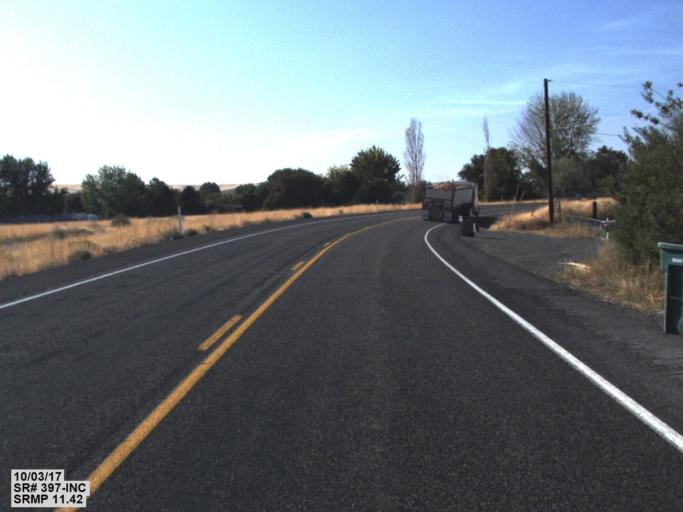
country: US
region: Washington
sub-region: Benton County
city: Finley
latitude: 46.1480
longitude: -119.0198
